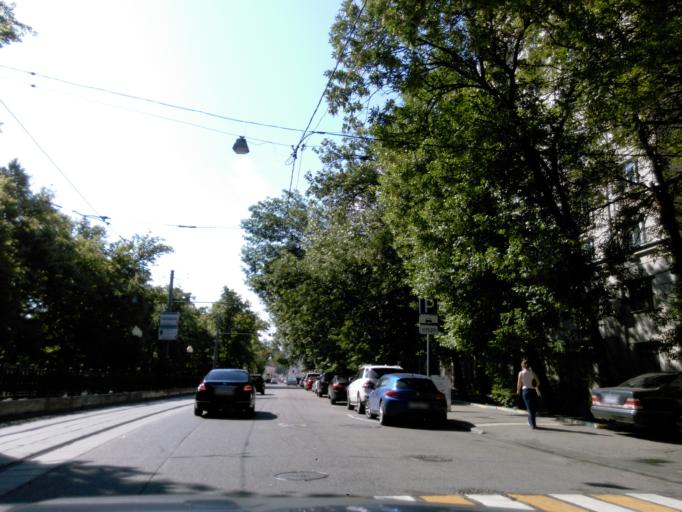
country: RU
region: Moscow
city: Moscow
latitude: 55.7618
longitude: 37.6434
